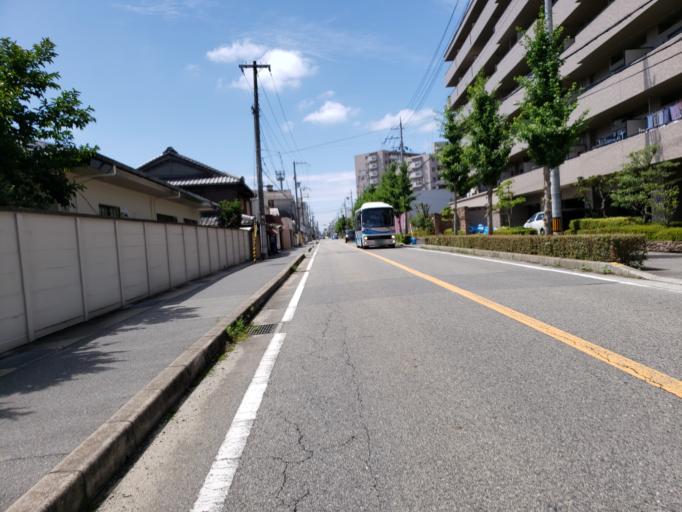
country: JP
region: Hyogo
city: Kakogawacho-honmachi
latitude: 34.7141
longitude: 134.8900
